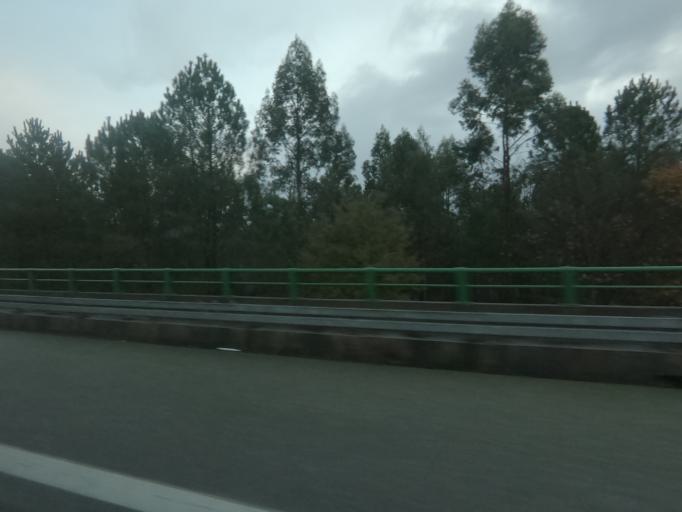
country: PT
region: Braga
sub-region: Barcelos
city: Galegos
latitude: 41.6341
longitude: -8.5618
